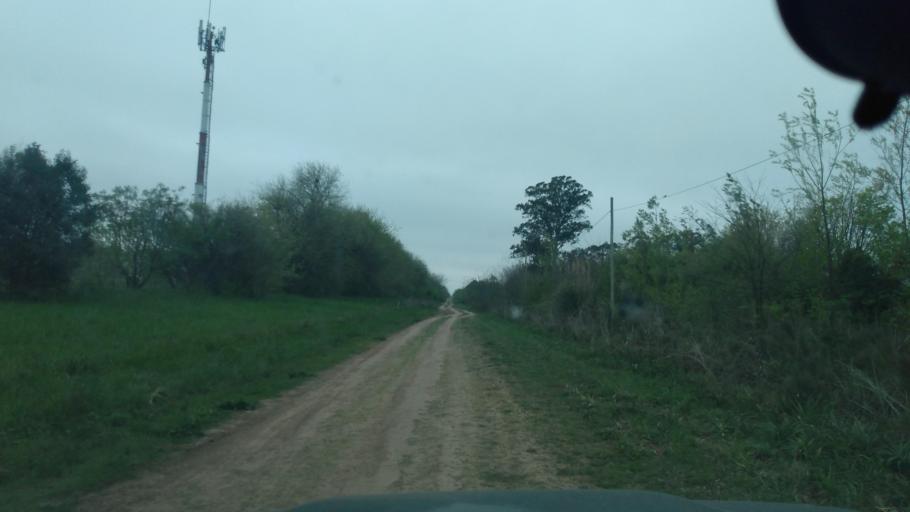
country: AR
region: Buenos Aires
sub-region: Partido de Lujan
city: Lujan
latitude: -34.5436
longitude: -59.2121
